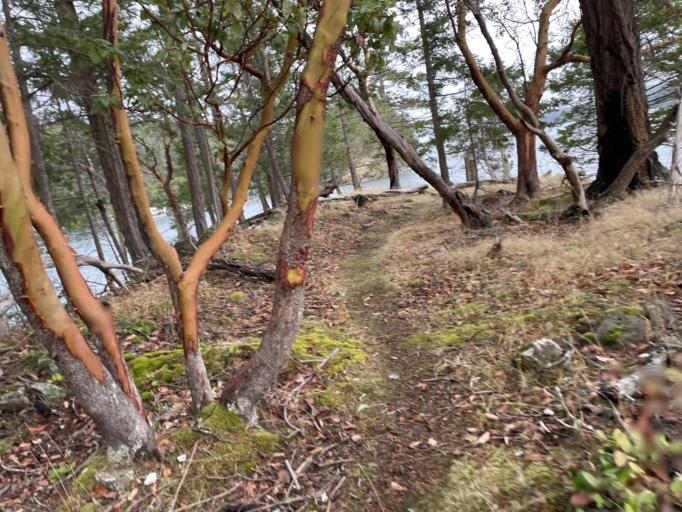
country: CA
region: British Columbia
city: North Cowichan
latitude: 48.9369
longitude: -123.5456
